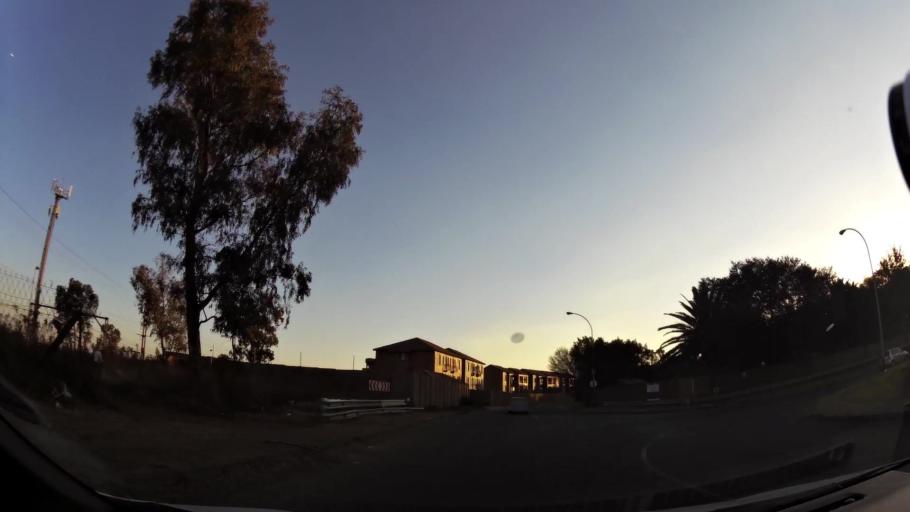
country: ZA
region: Gauteng
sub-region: Ekurhuleni Metropolitan Municipality
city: Germiston
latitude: -26.2572
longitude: 28.1722
